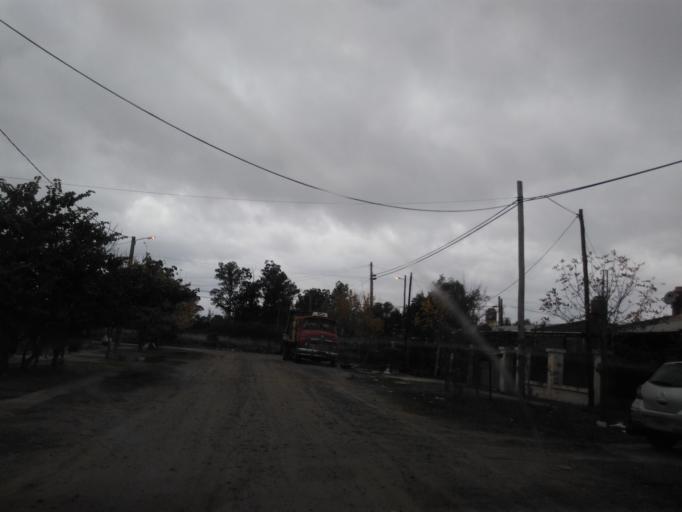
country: AR
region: Chaco
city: Fontana
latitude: -27.4590
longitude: -59.0419
